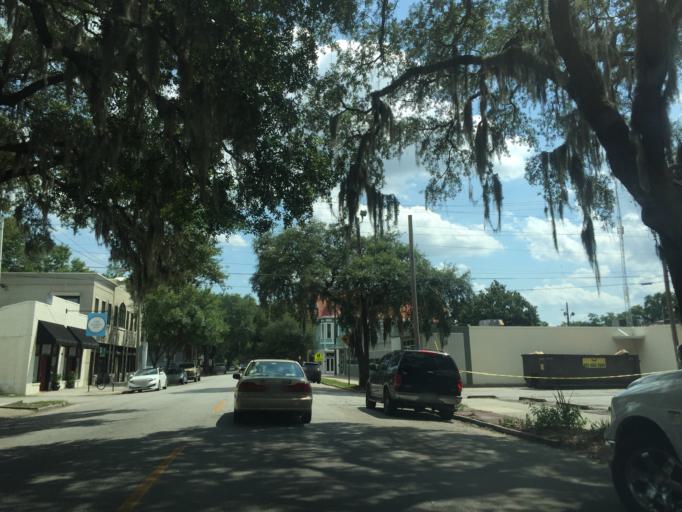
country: US
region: Georgia
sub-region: Chatham County
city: Savannah
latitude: 32.0616
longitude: -81.0985
